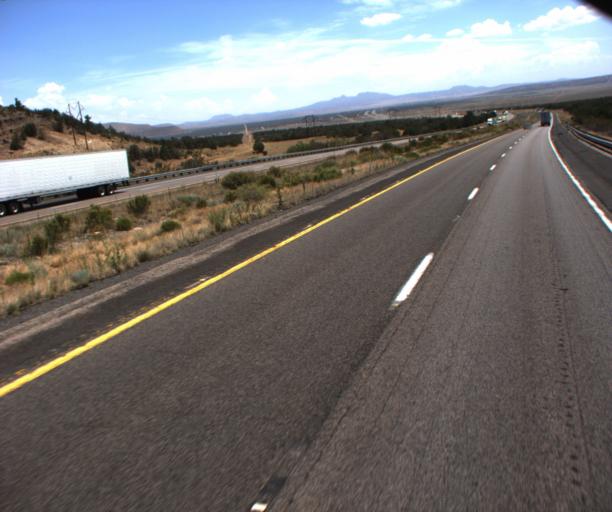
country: US
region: Arizona
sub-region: Mohave County
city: Peach Springs
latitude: 35.3020
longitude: -113.0137
